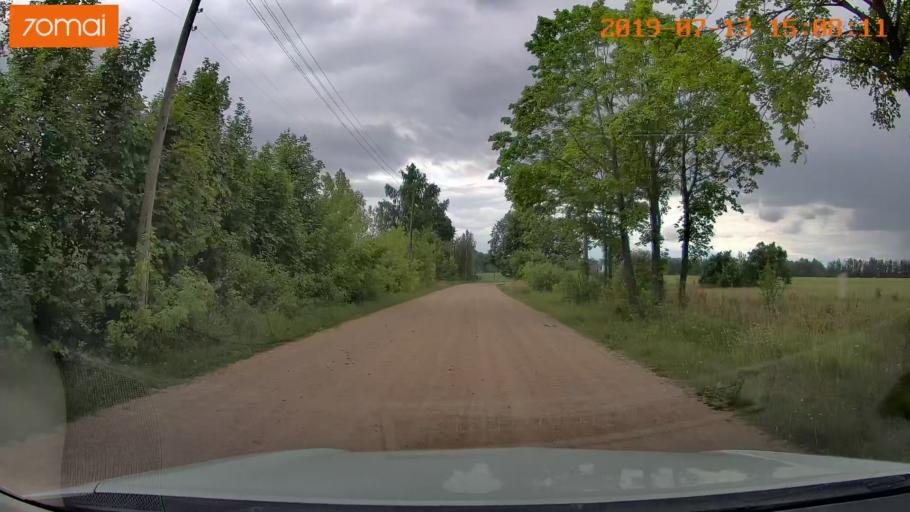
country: BY
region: Mogilev
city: Hlusha
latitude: 53.1813
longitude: 28.7574
